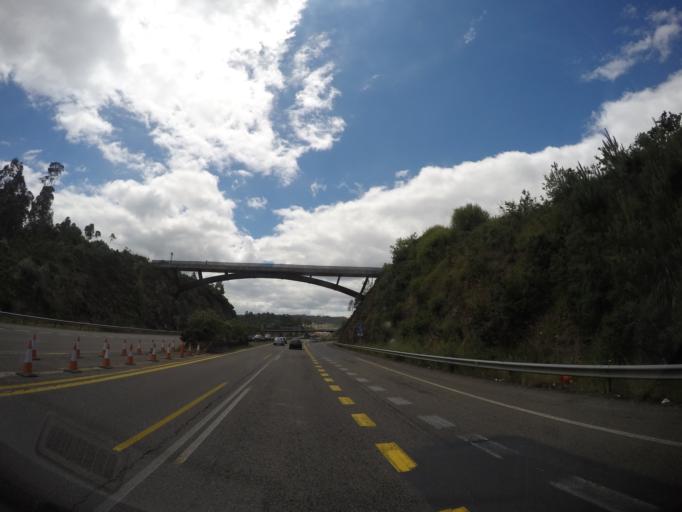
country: ES
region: Galicia
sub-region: Provincia da Coruna
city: Lousame
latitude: 42.8142
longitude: -8.7768
